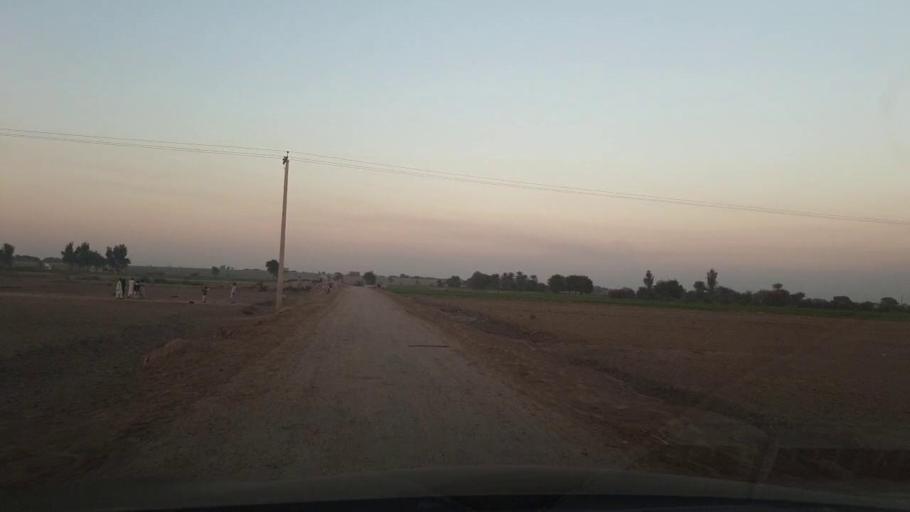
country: PK
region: Sindh
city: Ubauro
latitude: 28.1757
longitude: 69.6344
